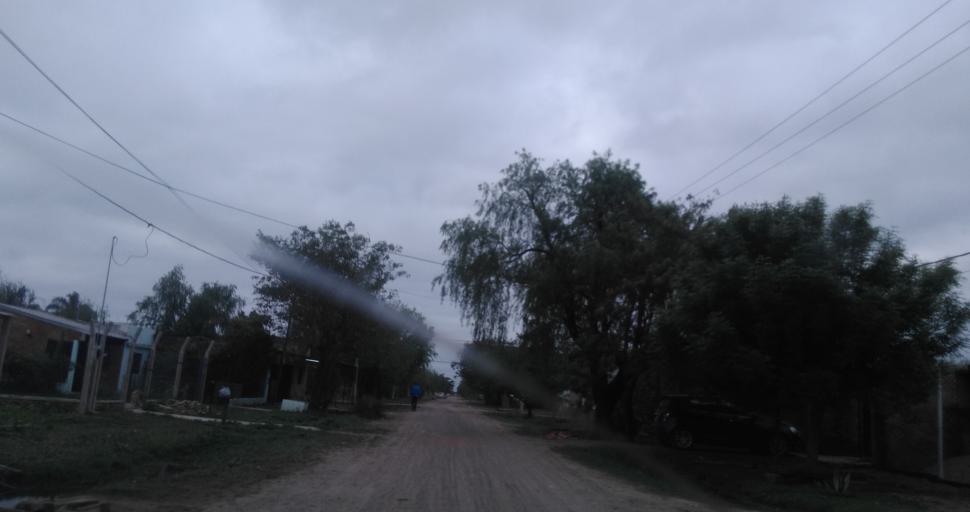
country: AR
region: Chaco
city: Resistencia
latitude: -27.4834
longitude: -58.9994
